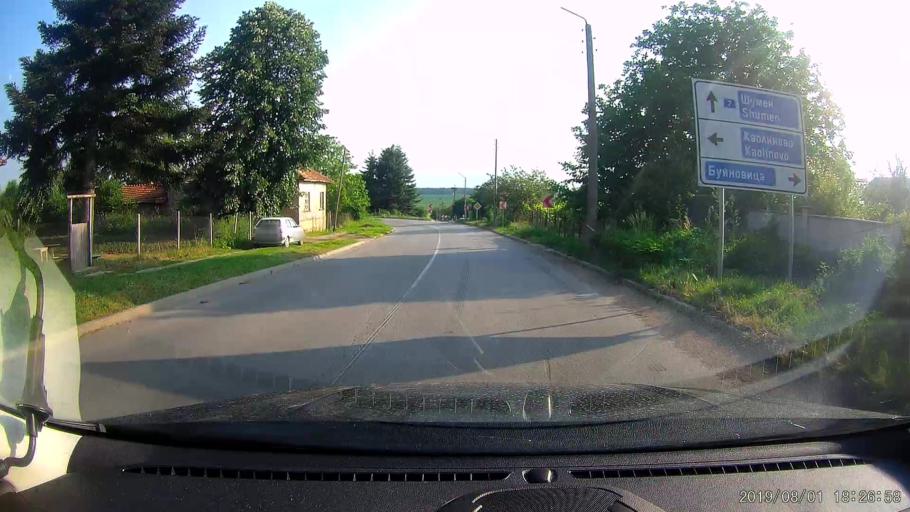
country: BG
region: Shumen
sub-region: Obshtina Venets
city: Venets
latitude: 43.5937
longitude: 26.9832
